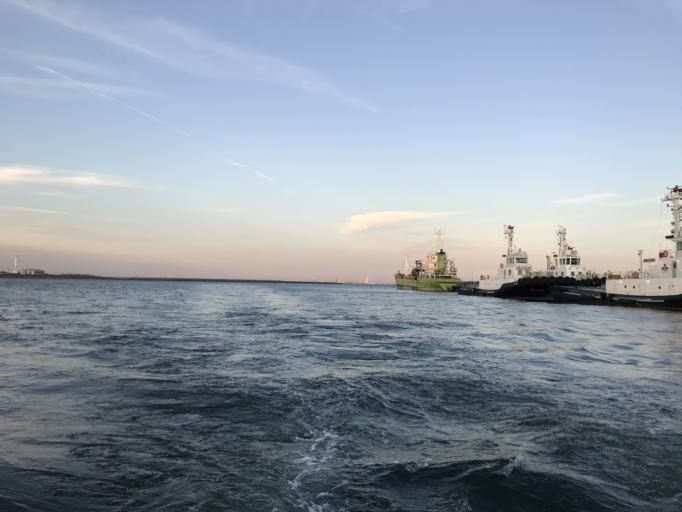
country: JP
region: Kanagawa
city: Yokosuka
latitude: 35.2844
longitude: 139.6751
